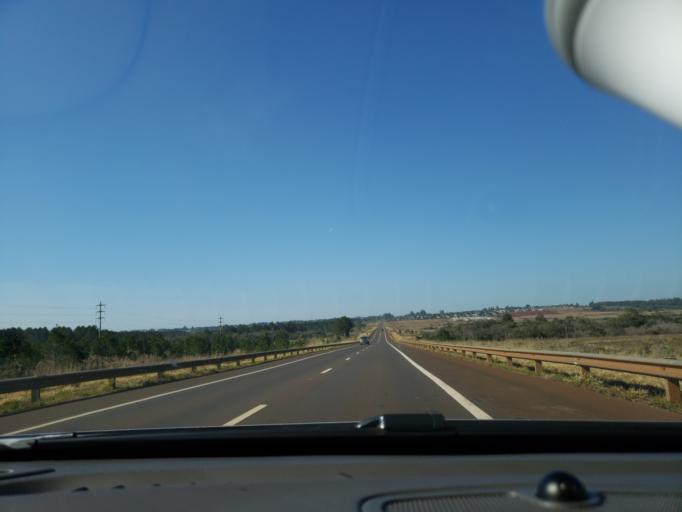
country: AR
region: Misiones
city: Garupa
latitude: -27.4648
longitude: -55.8996
